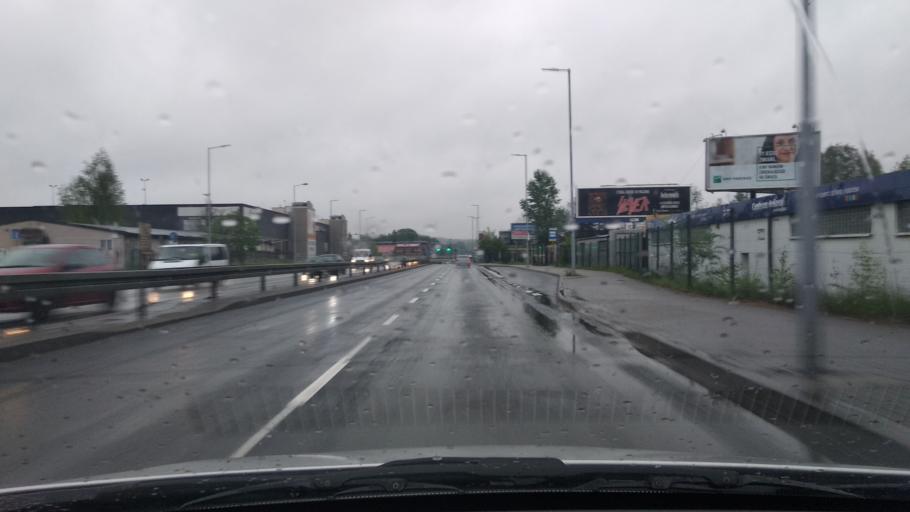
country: PL
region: Silesian Voivodeship
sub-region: Katowice
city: Katowice
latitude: 50.2613
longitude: 18.9864
